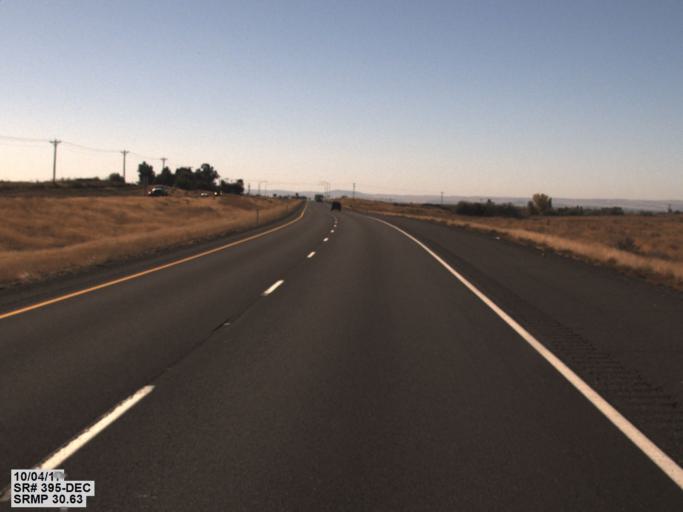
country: US
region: Washington
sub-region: Franklin County
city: Pasco
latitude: 46.3642
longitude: -119.0842
